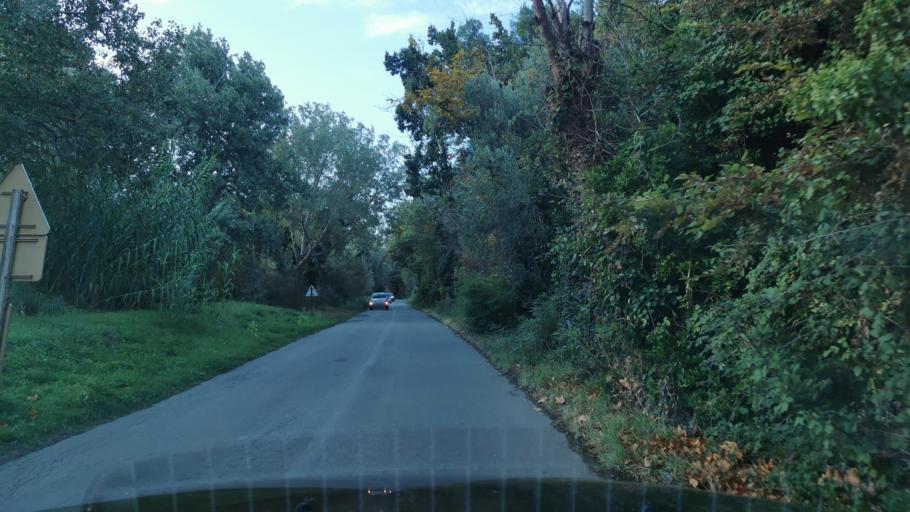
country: FR
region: Languedoc-Roussillon
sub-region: Departement de l'Aude
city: Gruissan
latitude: 43.1294
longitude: 3.0314
